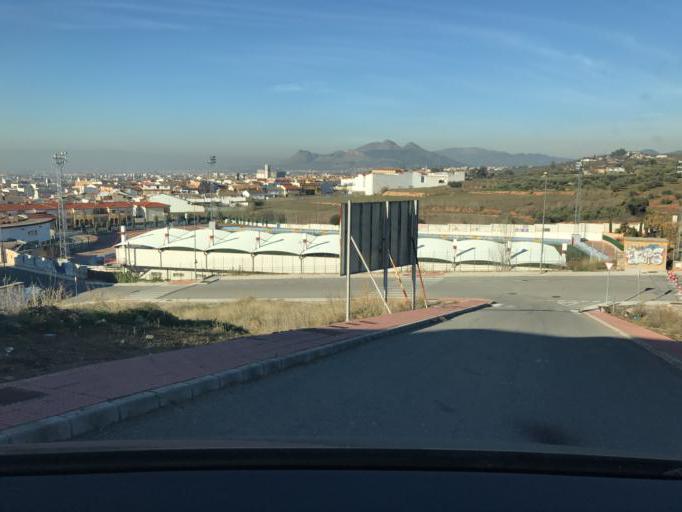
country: ES
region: Andalusia
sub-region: Provincia de Granada
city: Peligros
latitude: 37.2355
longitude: -3.6194
